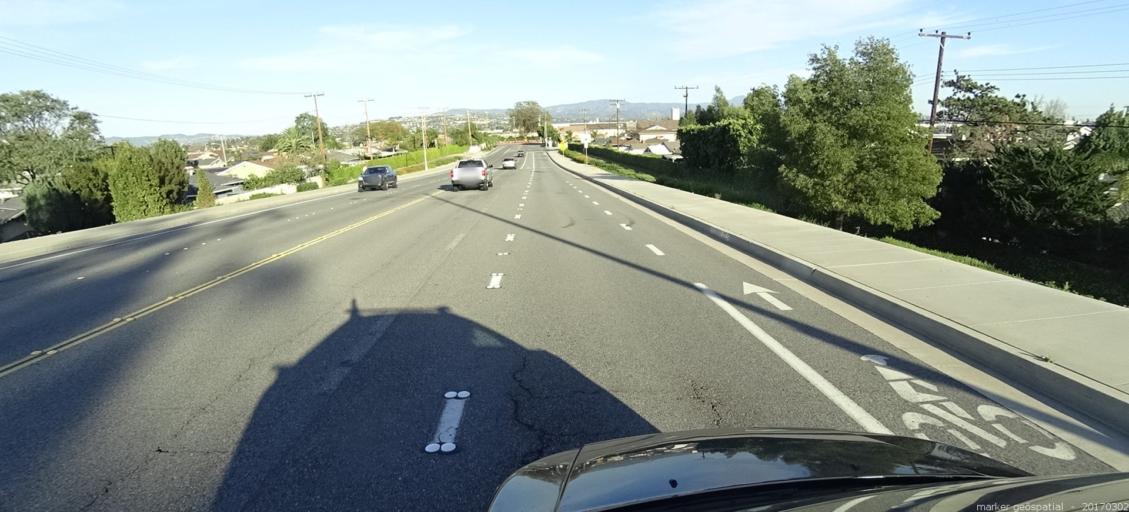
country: US
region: California
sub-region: Orange County
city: Anaheim
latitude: 33.8253
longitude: -117.8749
